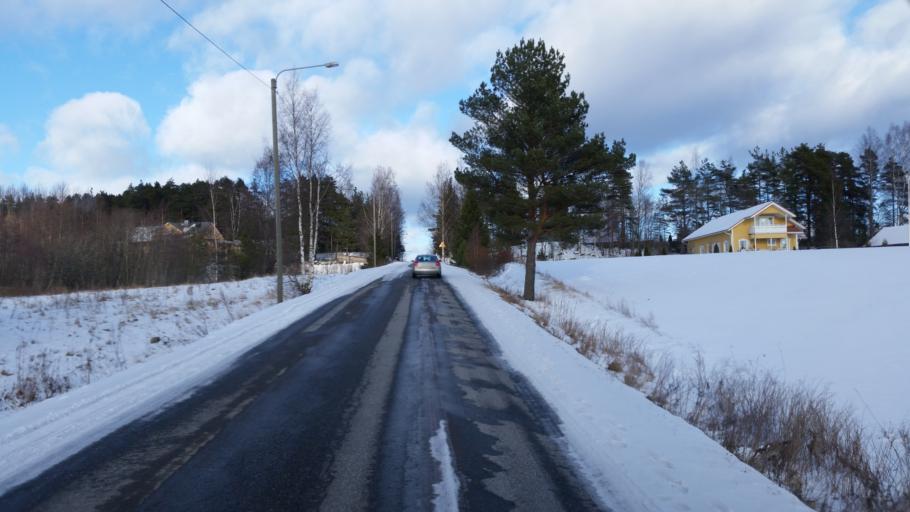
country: FI
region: Varsinais-Suomi
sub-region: Salo
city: Muurla
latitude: 60.3587
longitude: 23.2925
